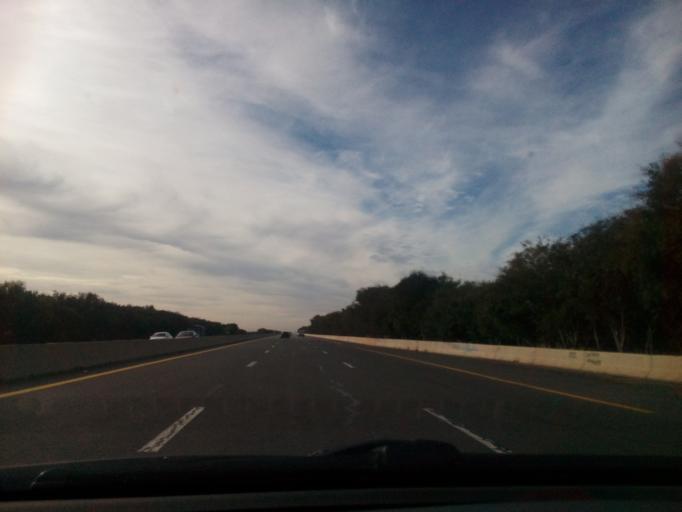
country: DZ
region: Sidi Bel Abbes
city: Sidi Bel Abbes
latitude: 35.2071
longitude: -0.6875
